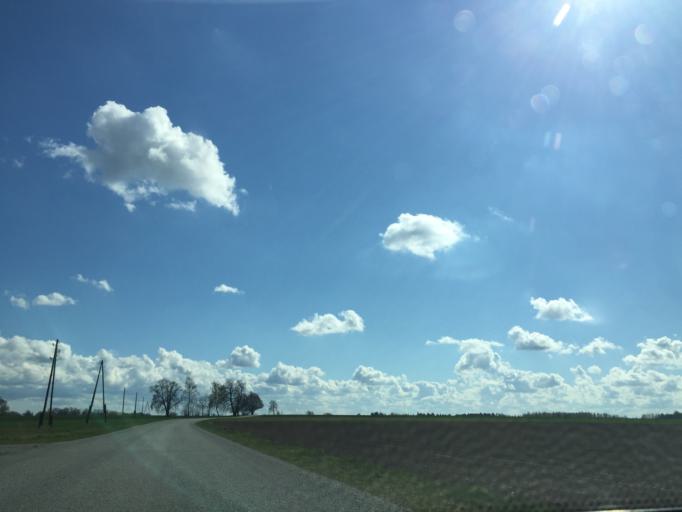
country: LV
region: Strenci
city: Strenci
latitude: 57.5213
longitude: 25.6820
